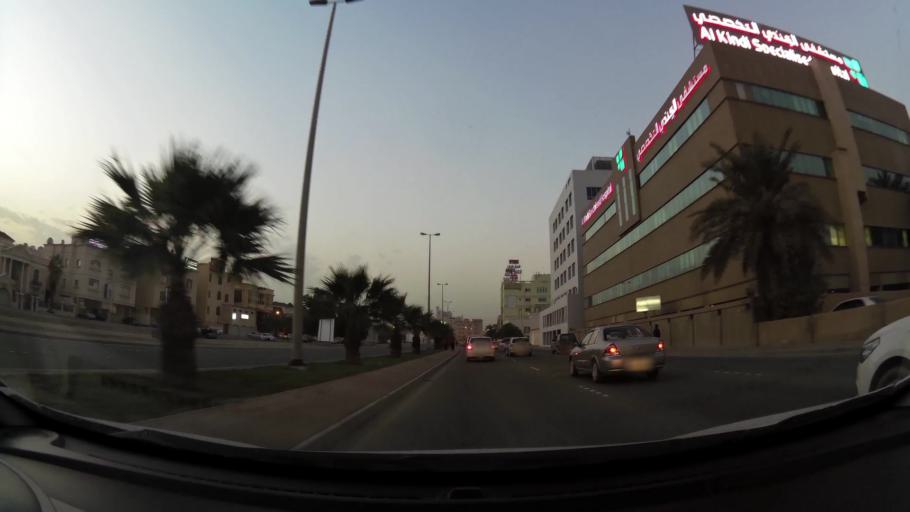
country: BH
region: Manama
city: Manama
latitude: 26.2089
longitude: 50.5668
